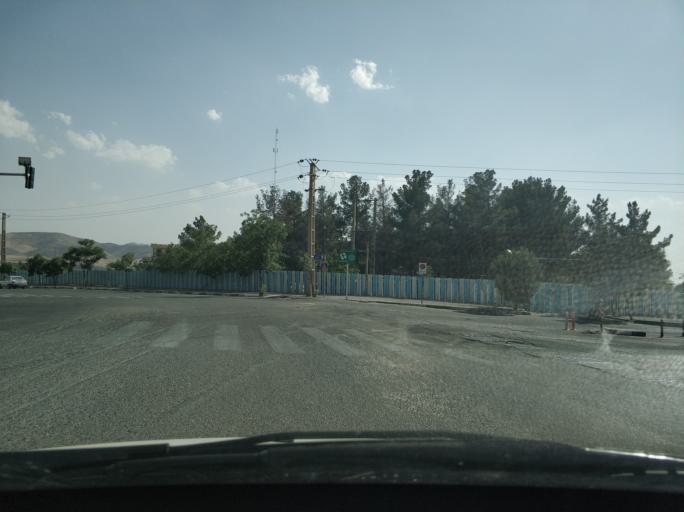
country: IR
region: Tehran
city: Tajrish
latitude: 35.7491
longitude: 51.5764
